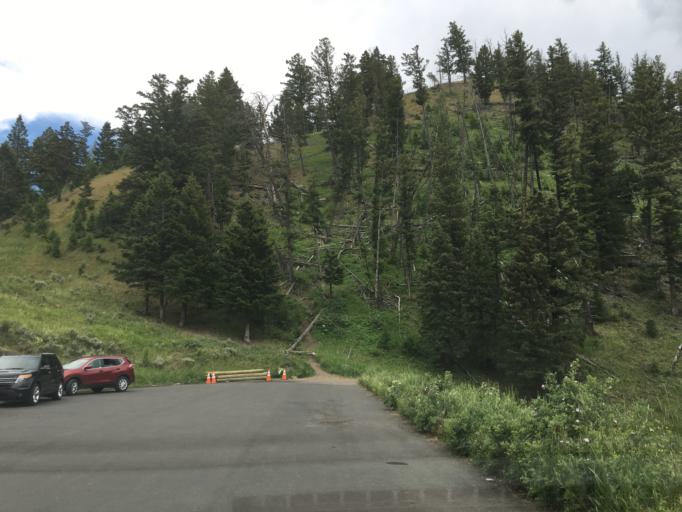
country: US
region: Montana
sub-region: Gallatin County
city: West Yellowstone
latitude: 44.9156
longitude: -110.4386
